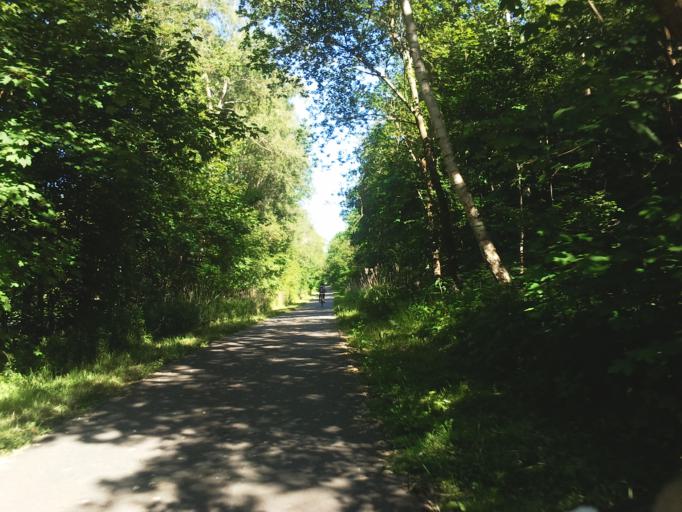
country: DE
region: Mecklenburg-Vorpommern
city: Nienhagen
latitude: 54.1908
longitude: 12.1830
